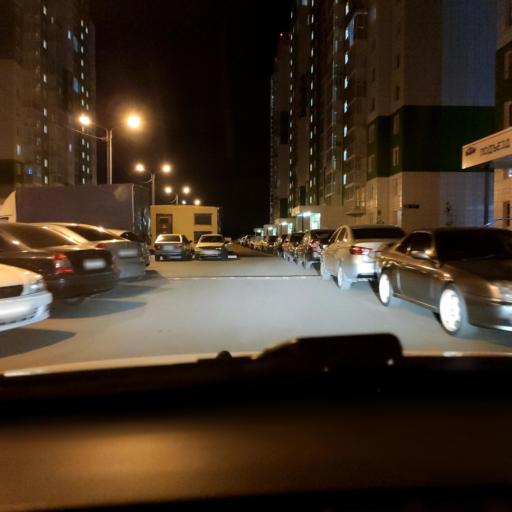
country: RU
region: Voronezj
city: Maslovka
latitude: 51.6349
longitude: 39.2960
